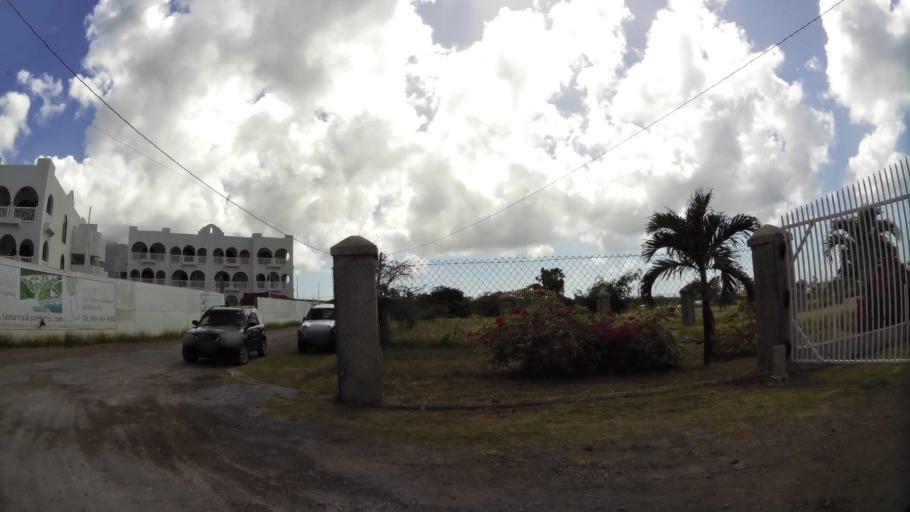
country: KN
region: Saint Thomas Lowland
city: Cotton Ground
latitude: 17.1873
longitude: -62.6182
